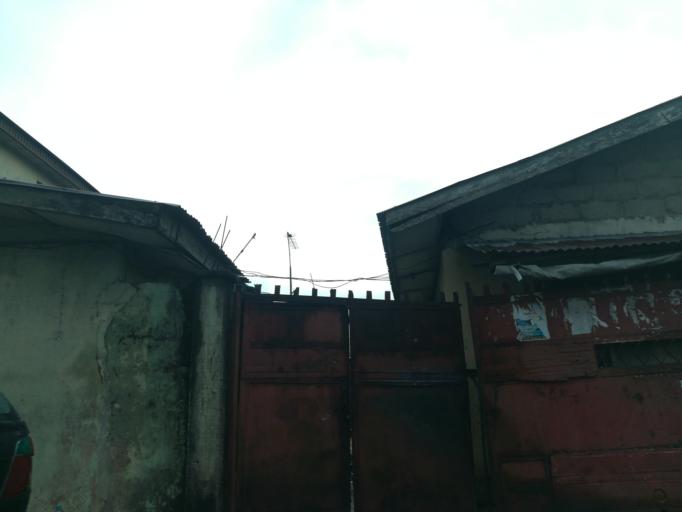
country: NG
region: Rivers
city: Port Harcourt
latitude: 4.7956
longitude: 6.9916
